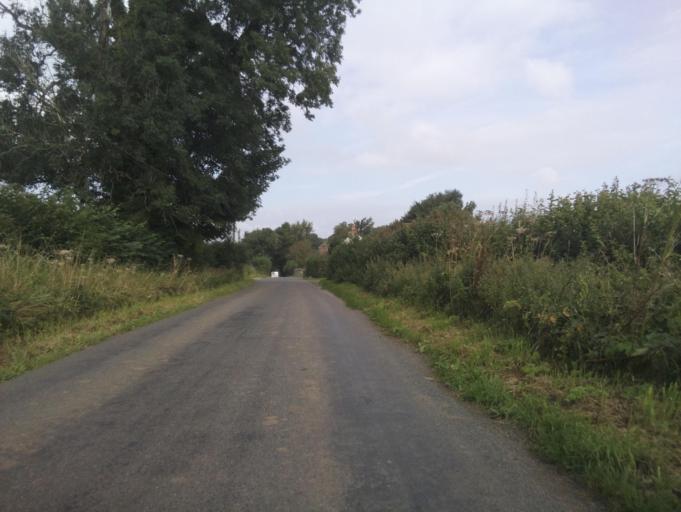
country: GB
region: England
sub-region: Bath and North East Somerset
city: East Harptree
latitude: 51.2677
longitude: -2.5834
